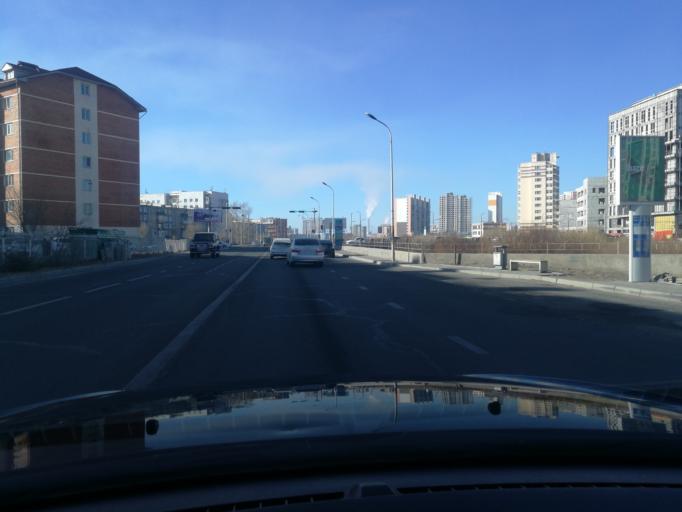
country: MN
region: Ulaanbaatar
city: Ulaanbaatar
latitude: 47.9052
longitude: 106.9083
